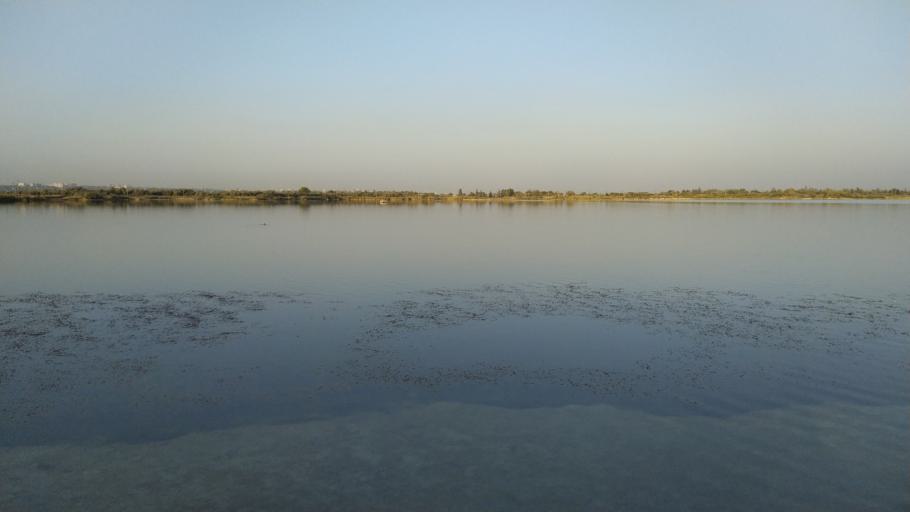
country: RU
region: Rostov
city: Bataysk
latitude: 47.1437
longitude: 39.6484
